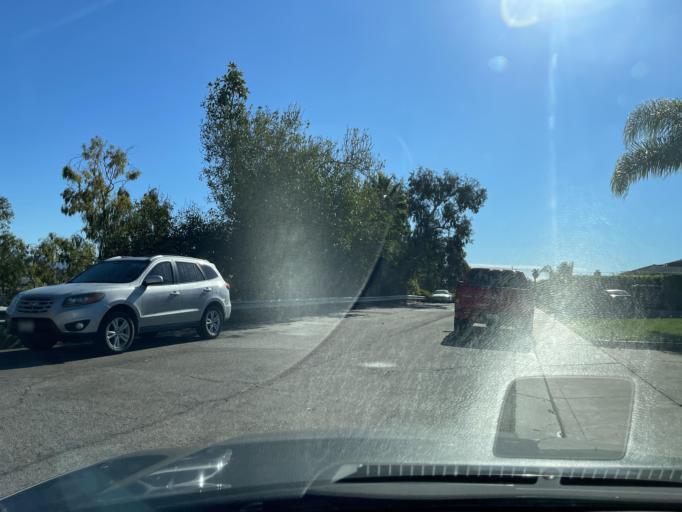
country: US
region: California
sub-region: San Diego County
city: National City
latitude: 32.6750
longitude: -117.0931
